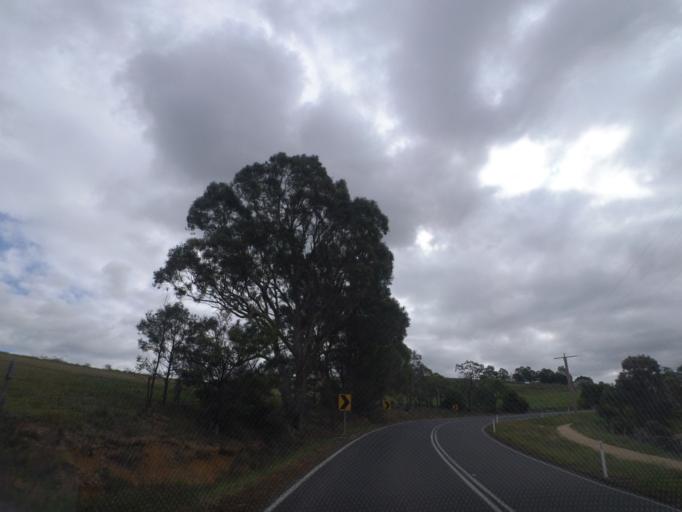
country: AU
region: Victoria
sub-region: Whittlesea
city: Whittlesea
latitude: -37.5257
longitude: 145.1082
